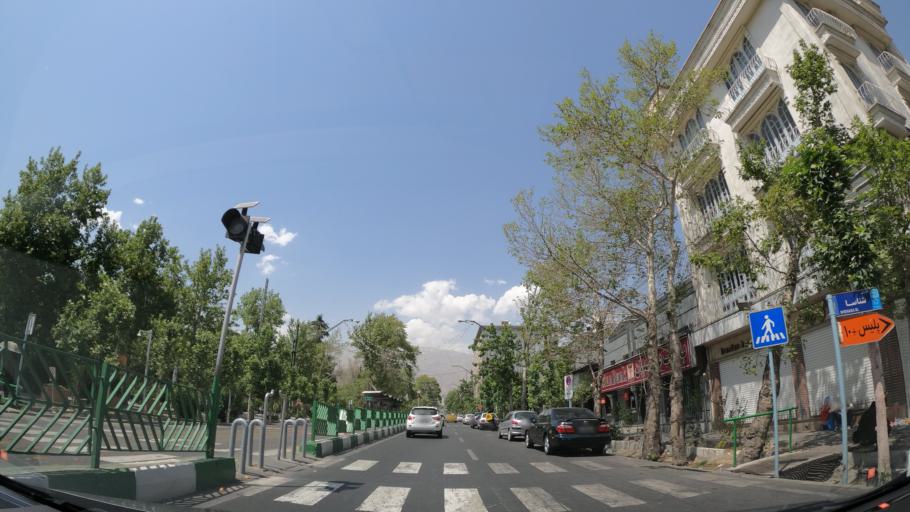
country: IR
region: Tehran
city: Tajrish
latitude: 35.7774
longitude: 51.4133
